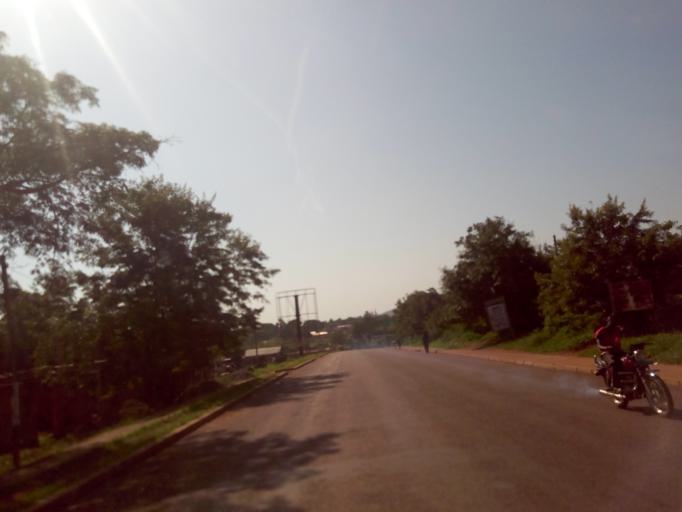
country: UG
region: Western Region
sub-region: Masindi District
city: Masindi
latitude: 1.6810
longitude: 31.7266
